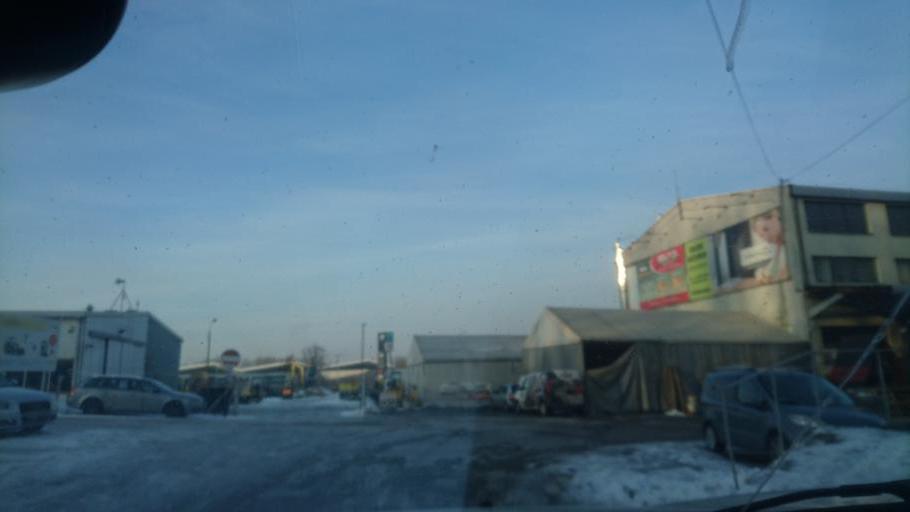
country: PL
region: Silesian Voivodeship
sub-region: Sosnowiec
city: Sosnowiec
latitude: 50.2488
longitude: 19.1205
